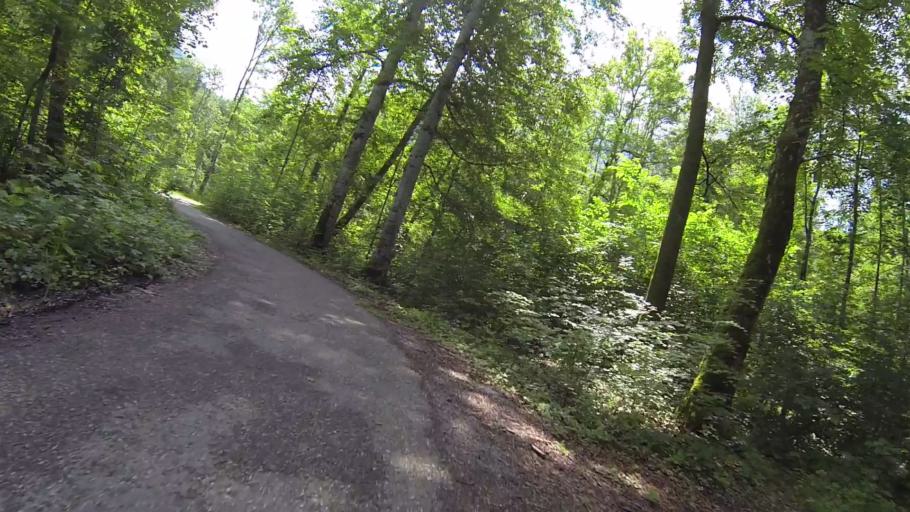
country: DE
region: Bavaria
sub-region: Swabia
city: Schwangau
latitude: 47.5578
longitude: 10.7345
